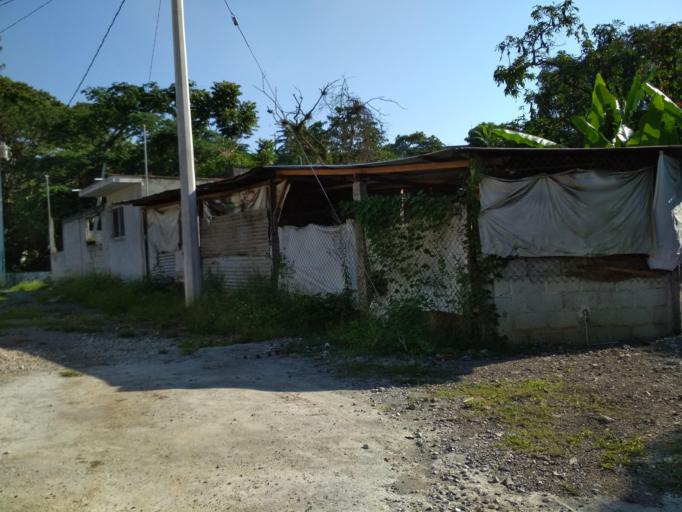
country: MX
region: Veracruz
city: Amatlan de los Reyes
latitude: 18.8662
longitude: -96.9186
